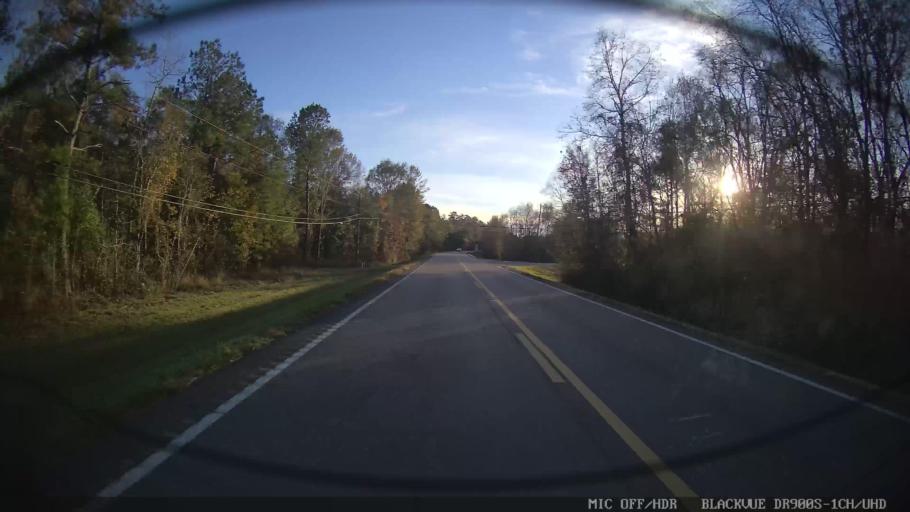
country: US
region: Mississippi
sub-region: Lamar County
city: Lumberton
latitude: 30.9942
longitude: -89.4556
